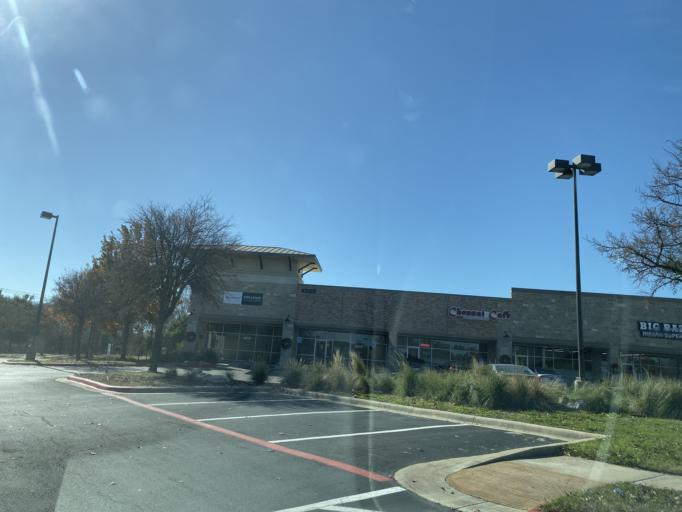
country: US
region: Texas
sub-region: Travis County
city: Windemere
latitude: 30.4761
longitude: -97.6700
